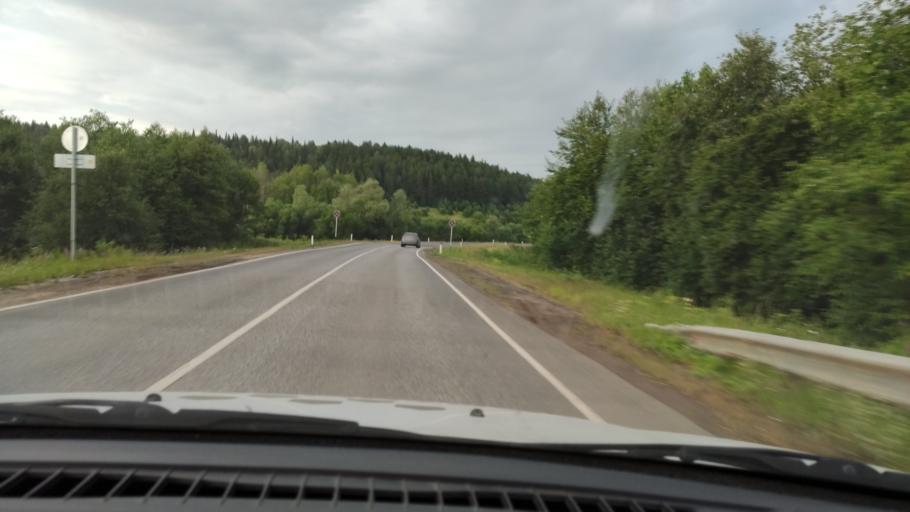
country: RU
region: Perm
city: Kukushtan
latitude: 57.4851
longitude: 56.6079
